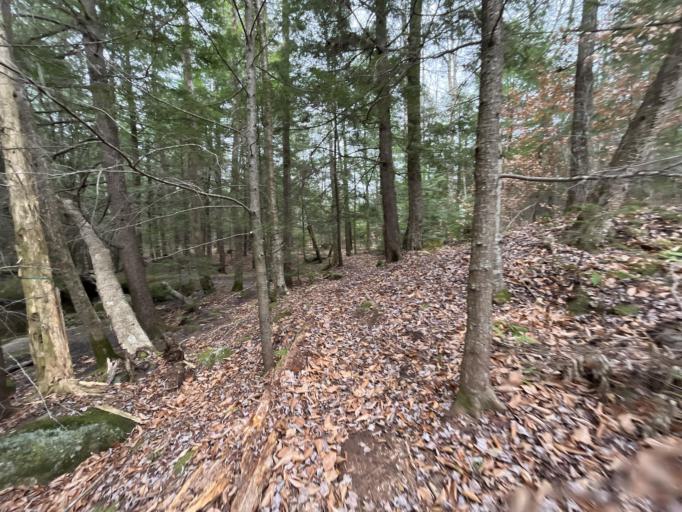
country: US
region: New Hampshire
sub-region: Merrimack County
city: New London
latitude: 43.3971
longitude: -71.9741
